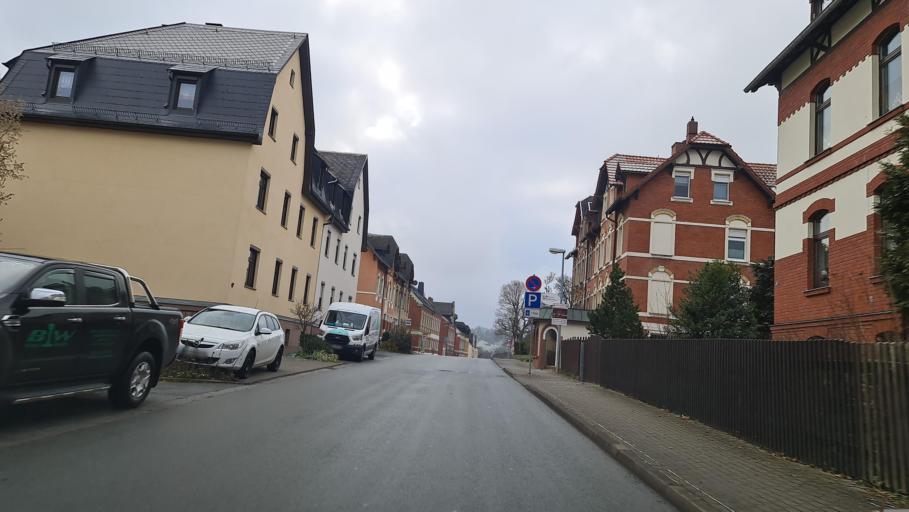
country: DE
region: Saxony
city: Weischlitz
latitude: 50.4499
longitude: 12.0580
